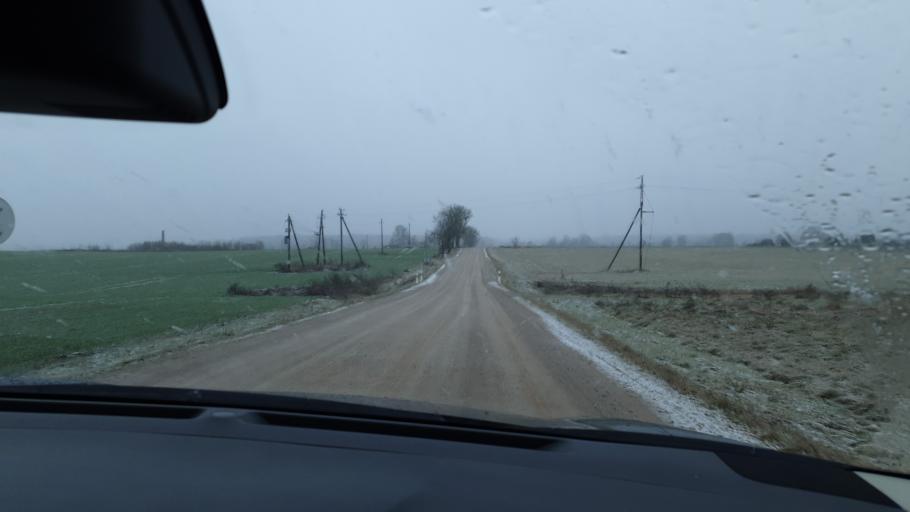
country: LT
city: Jieznas
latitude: 54.5820
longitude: 24.3165
